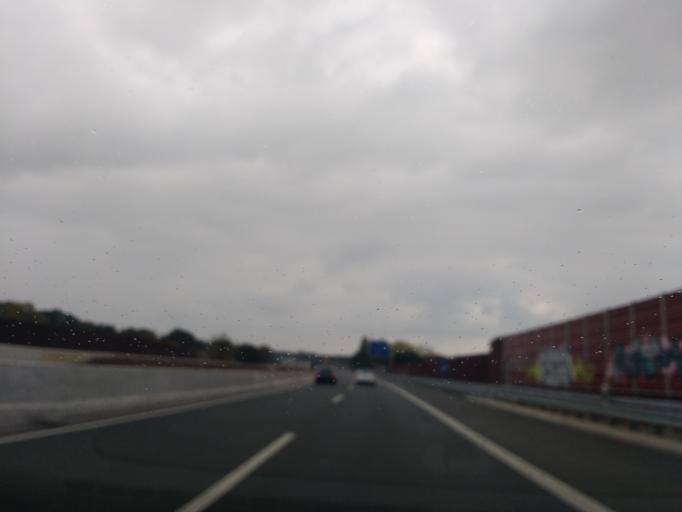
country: DE
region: North Rhine-Westphalia
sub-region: Regierungsbezirk Detmold
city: Steinhagen
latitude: 51.9766
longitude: 8.4694
